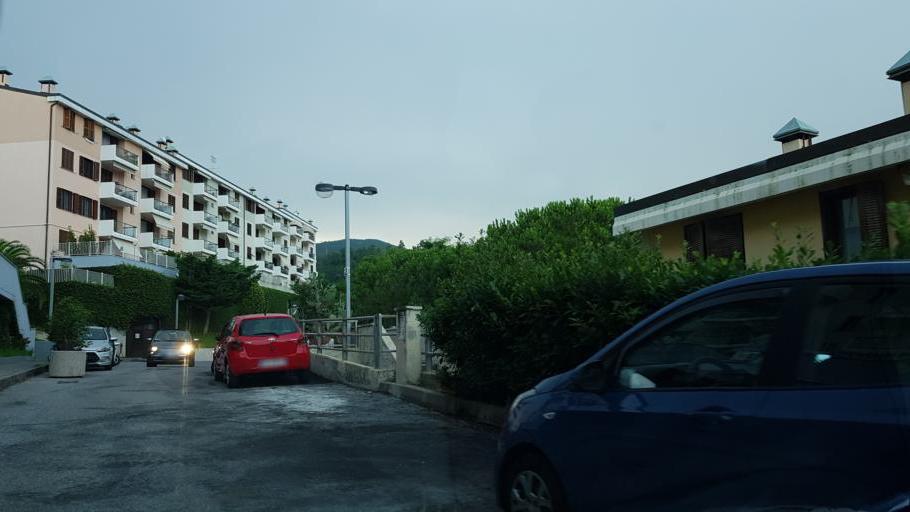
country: IT
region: Liguria
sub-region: Provincia di Genova
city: San Teodoro
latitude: 44.4309
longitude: 8.8308
